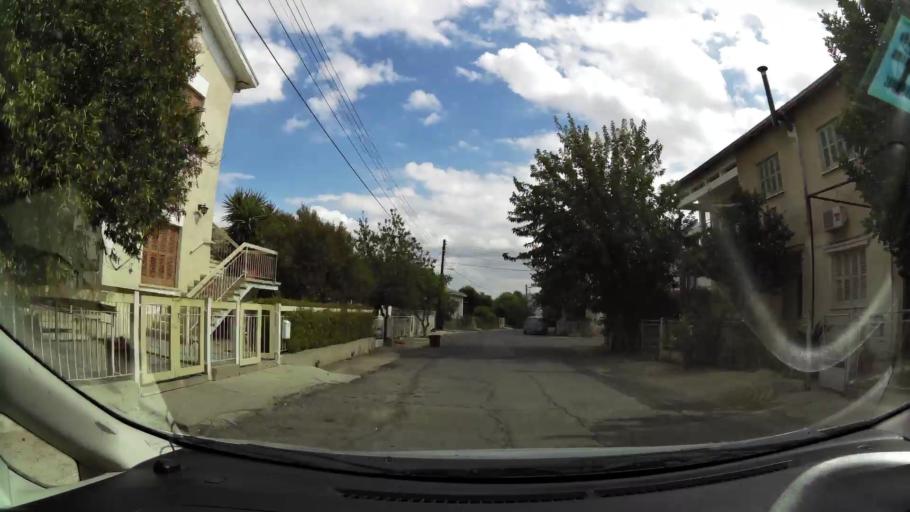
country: CY
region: Lefkosia
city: Nicosia
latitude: 35.1772
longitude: 33.3771
